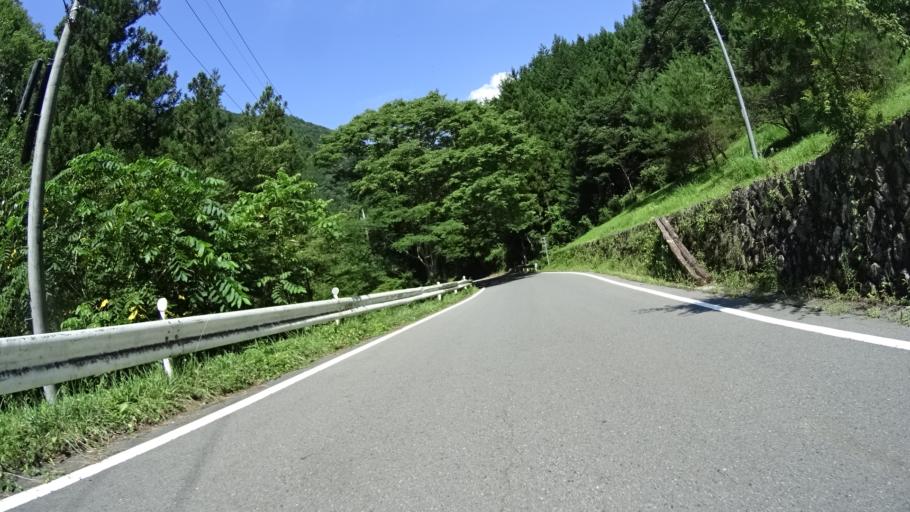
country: JP
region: Gunma
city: Tomioka
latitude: 36.0737
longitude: 138.8290
